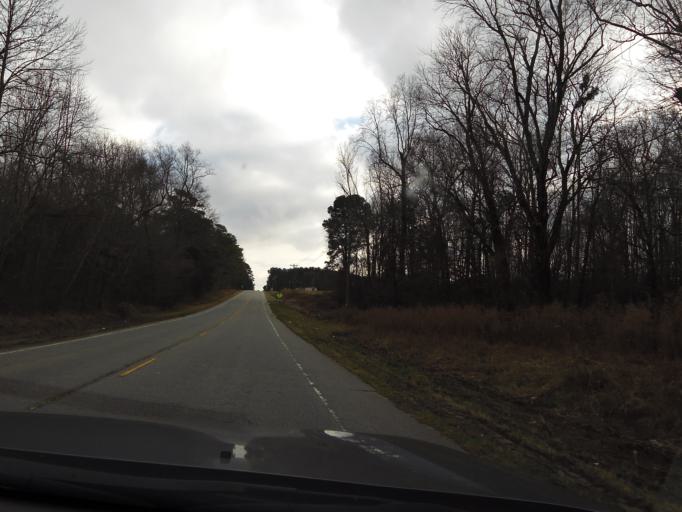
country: US
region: North Carolina
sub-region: Edgecombe County
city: Pinetops
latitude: 35.8426
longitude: -77.6622
